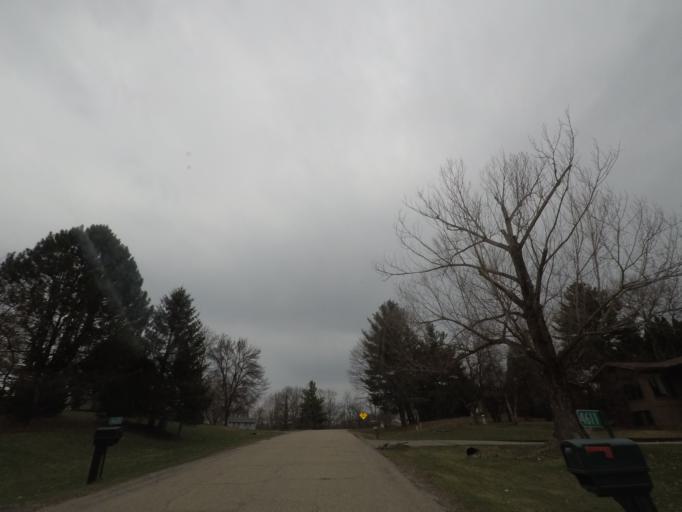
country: US
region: Wisconsin
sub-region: Dane County
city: Middleton
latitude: 43.1075
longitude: -89.5478
